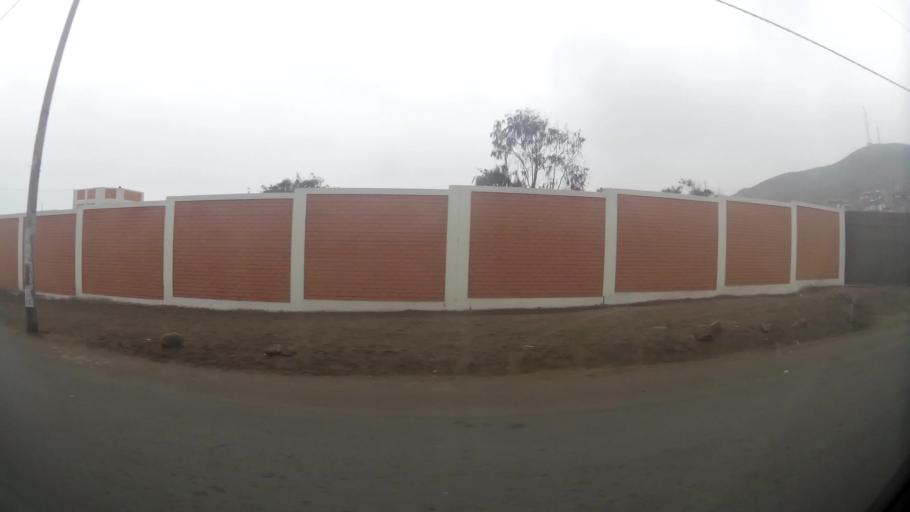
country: PE
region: Lima
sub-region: Provincia de Huaral
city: Chancay
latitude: -11.5870
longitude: -77.2701
